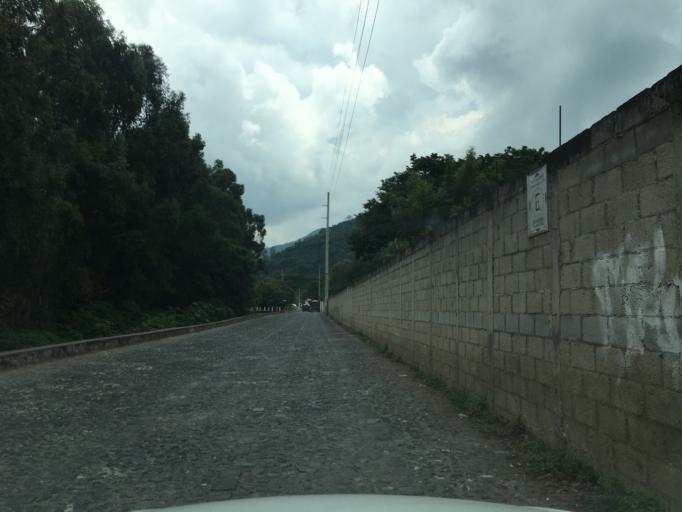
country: GT
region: Sacatepequez
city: Antigua Guatemala
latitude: 14.5472
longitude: -90.7318
